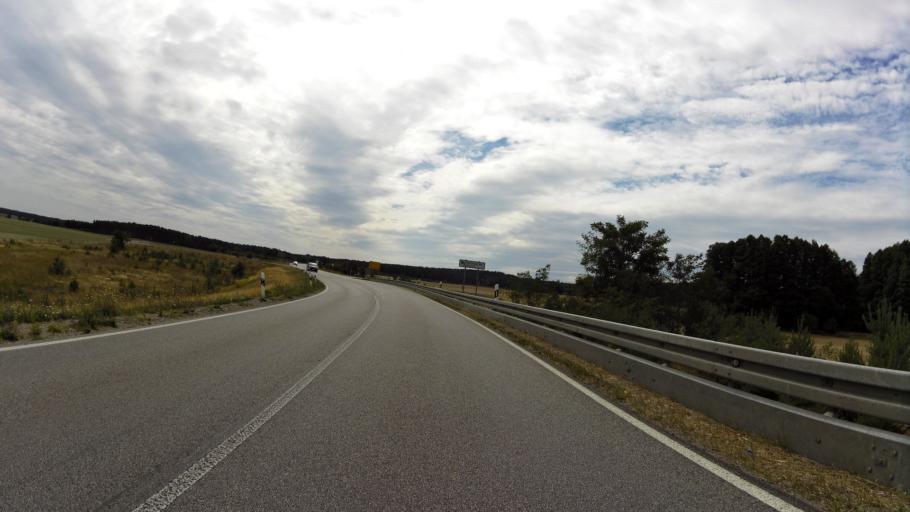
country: DE
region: Brandenburg
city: Neuzelle
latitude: 52.0706
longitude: 14.6614
